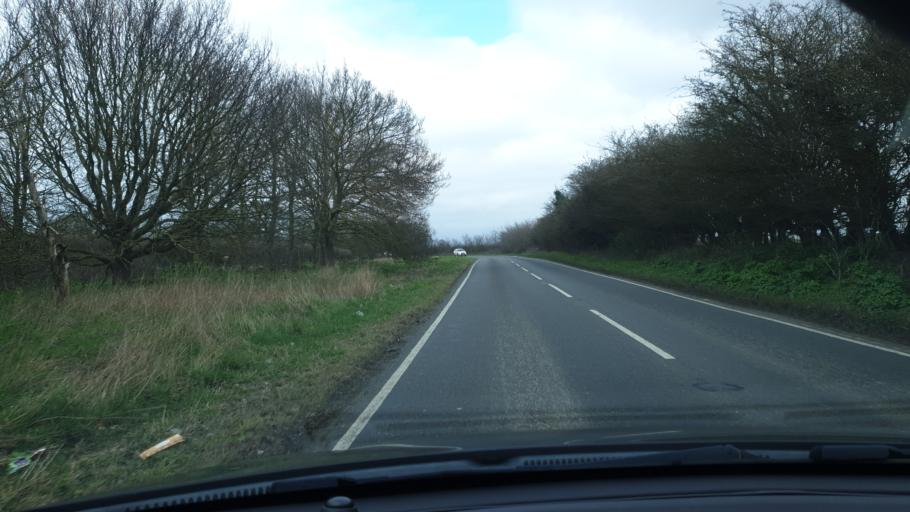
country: GB
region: England
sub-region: Essex
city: Frinton-on-Sea
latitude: 51.8202
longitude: 1.2078
